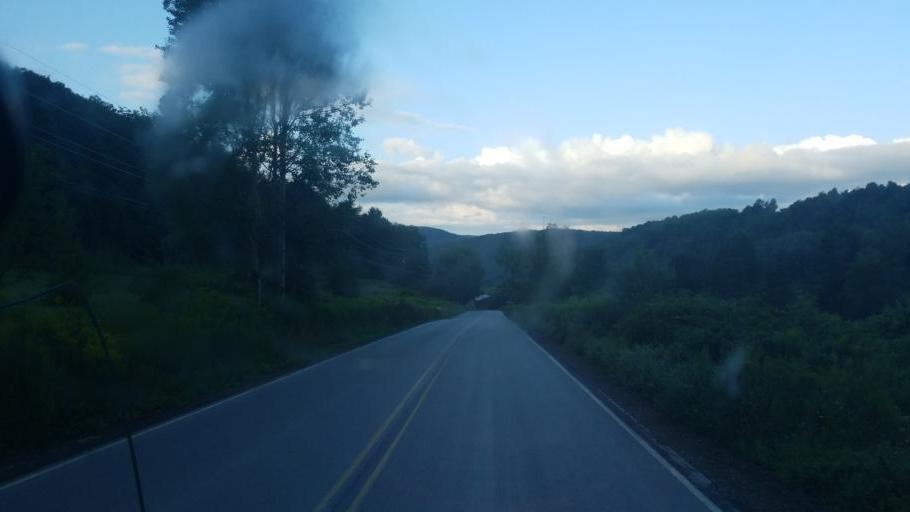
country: US
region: Pennsylvania
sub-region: Potter County
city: Galeton
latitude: 41.8450
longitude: -77.7819
